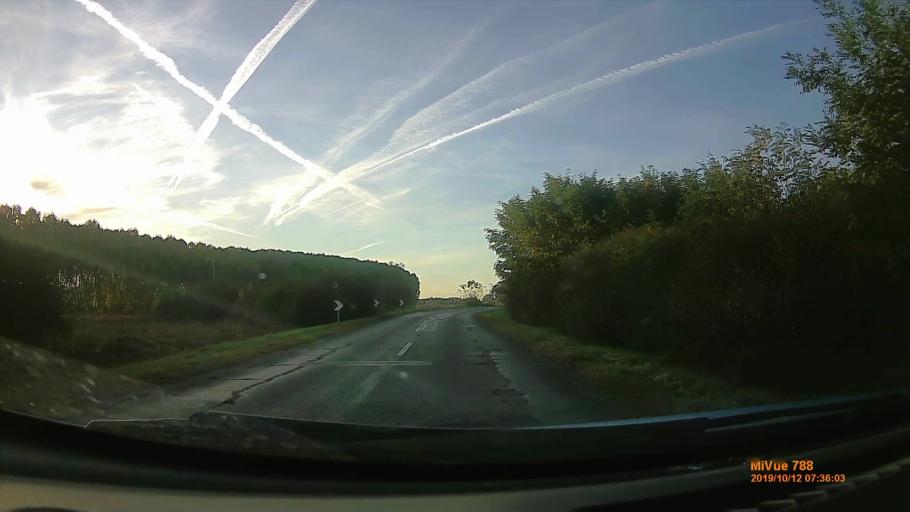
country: HU
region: Hajdu-Bihar
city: Pocsaj
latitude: 47.2485
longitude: 21.8120
